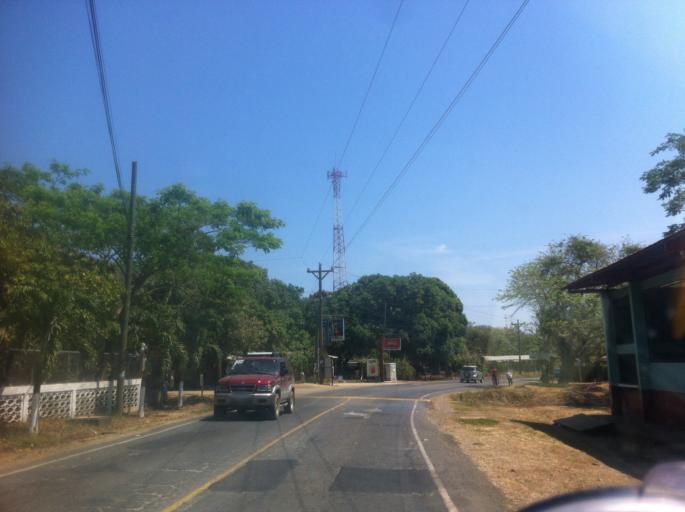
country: CR
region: Guanacaste
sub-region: Canton de Nicoya
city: Nicoya
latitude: 10.1142
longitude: -85.4516
